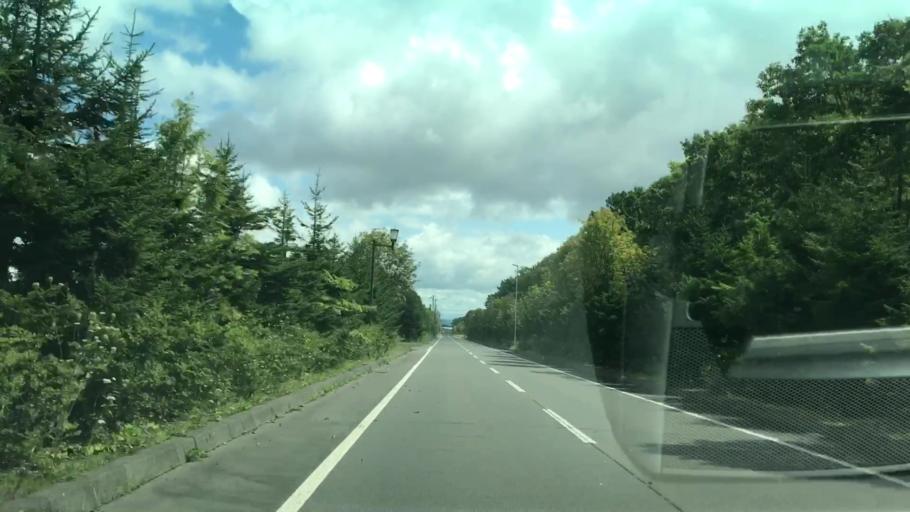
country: JP
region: Hokkaido
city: Chitose
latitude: 42.7777
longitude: 141.6063
